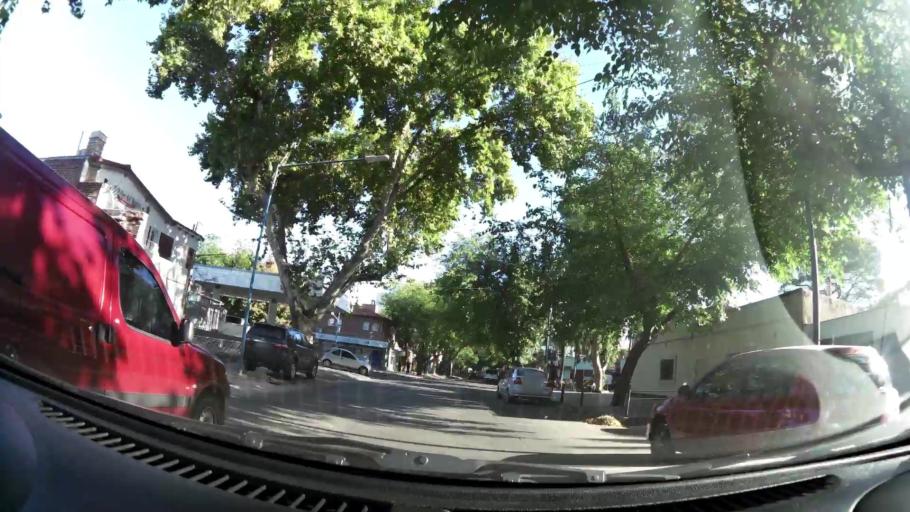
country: AR
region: Mendoza
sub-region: Departamento de Godoy Cruz
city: Godoy Cruz
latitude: -32.9085
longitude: -68.8514
